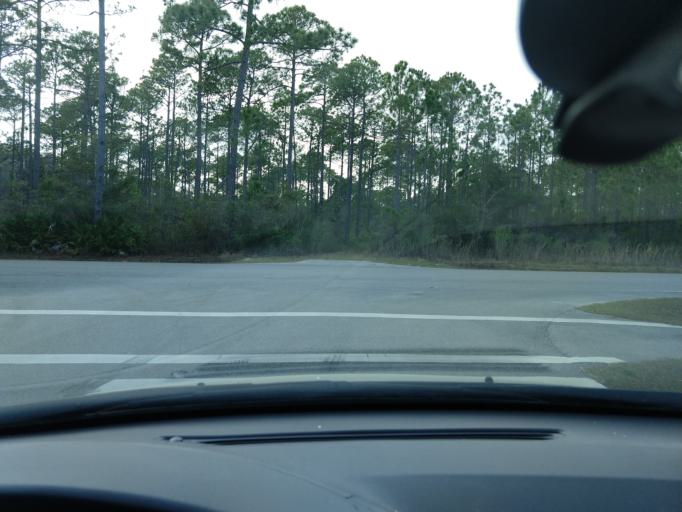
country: US
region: Florida
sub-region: Walton County
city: Seaside
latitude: 30.3791
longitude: -86.1869
